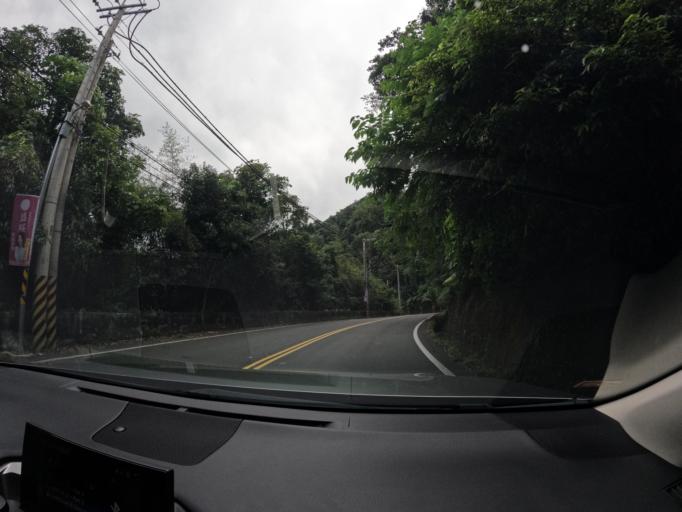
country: TW
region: Taiwan
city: Fengyuan
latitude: 24.3139
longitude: 120.8724
